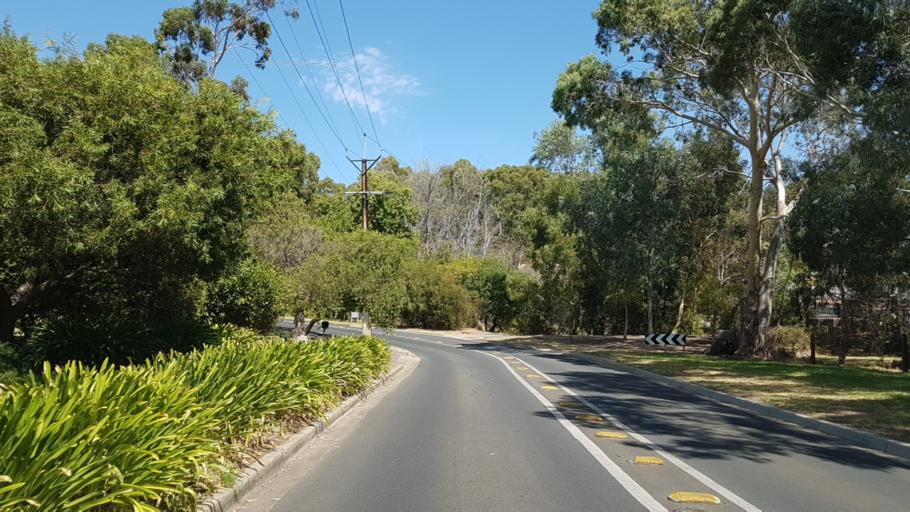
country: AU
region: South Australia
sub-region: Mitcham
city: Mitcham
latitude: -34.9824
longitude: 138.6242
